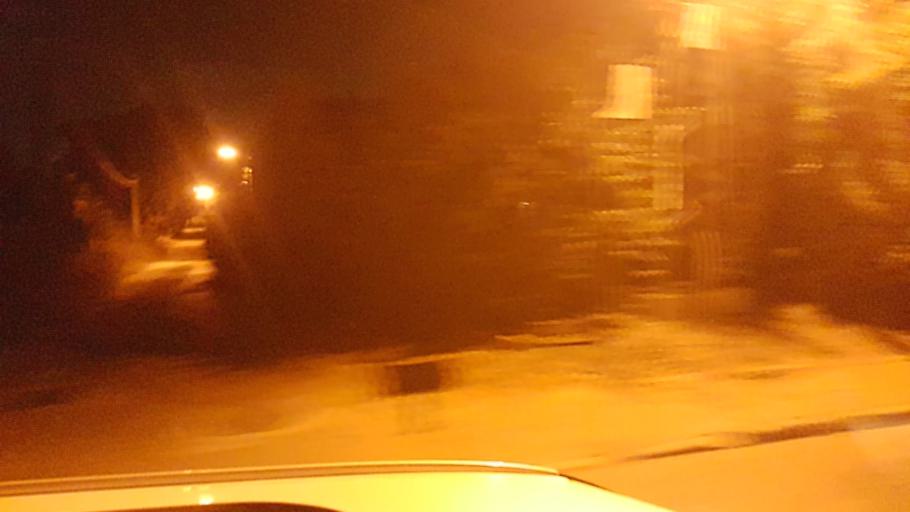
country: IL
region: Central District
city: Hod HaSharon
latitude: 32.1625
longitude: 34.8836
